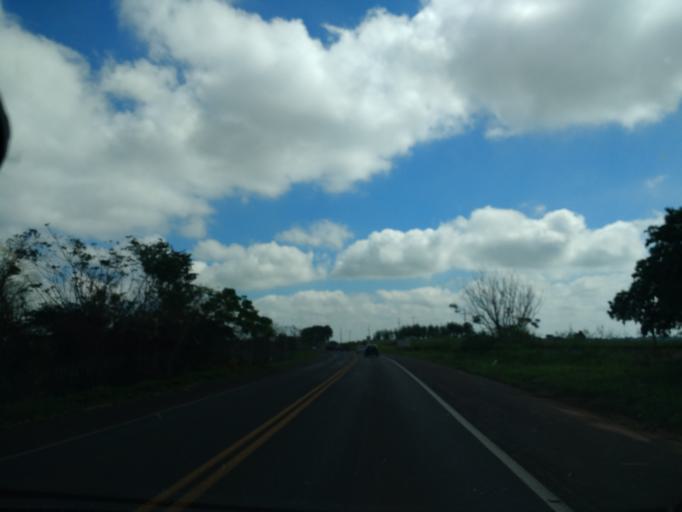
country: BR
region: Parana
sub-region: Cruzeiro Do Oeste
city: Cruzeiro do Oeste
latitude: -23.7668
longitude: -53.1155
